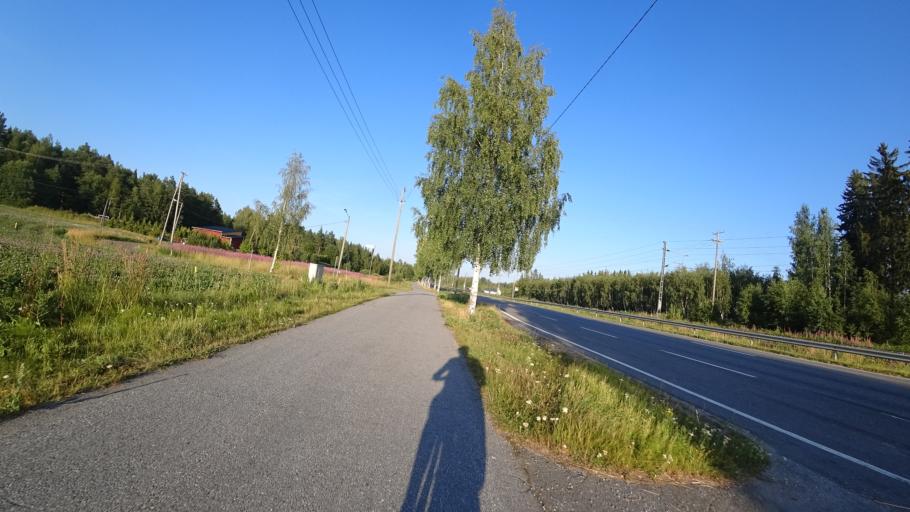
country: FI
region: Pirkanmaa
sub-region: Tampere
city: Nokia
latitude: 61.4672
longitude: 23.4065
